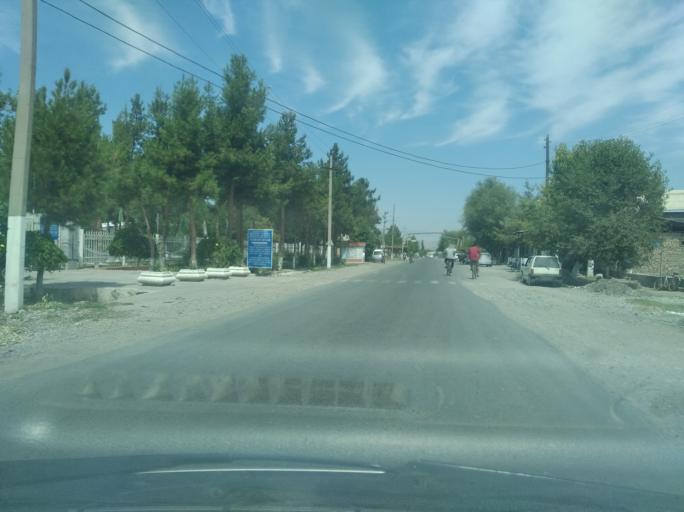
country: KG
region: Osh
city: Aravan
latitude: 40.6121
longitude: 72.4564
